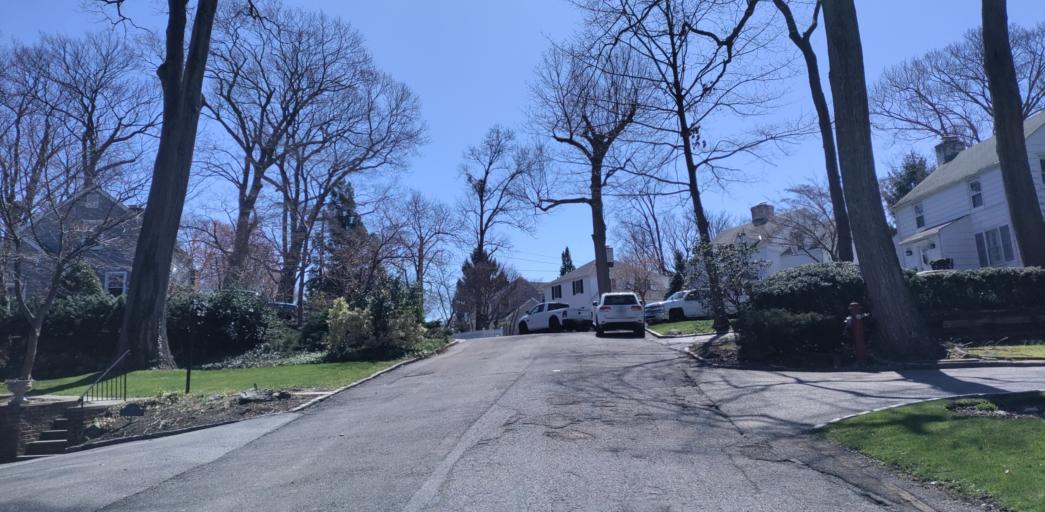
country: US
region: New York
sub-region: Nassau County
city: Glenwood Landing
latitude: 40.8345
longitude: -73.6337
